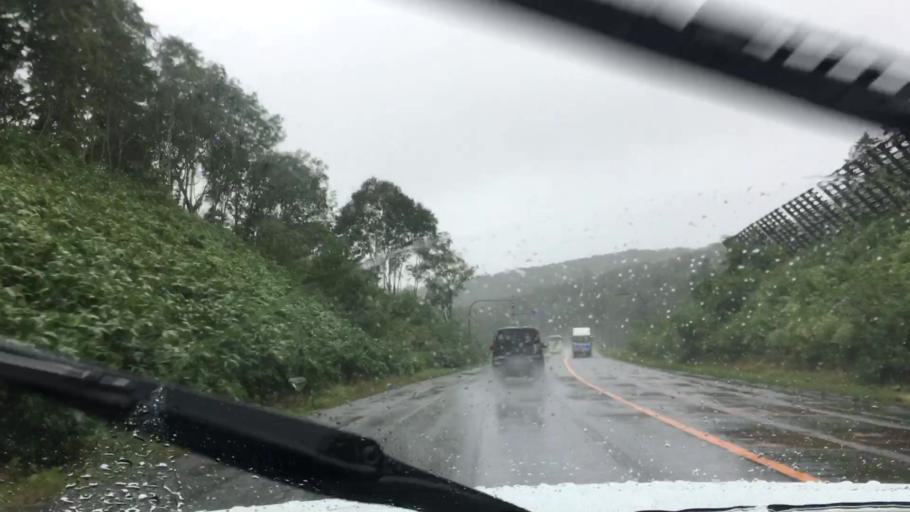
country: JP
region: Hokkaido
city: Sapporo
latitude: 42.8648
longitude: 141.1085
